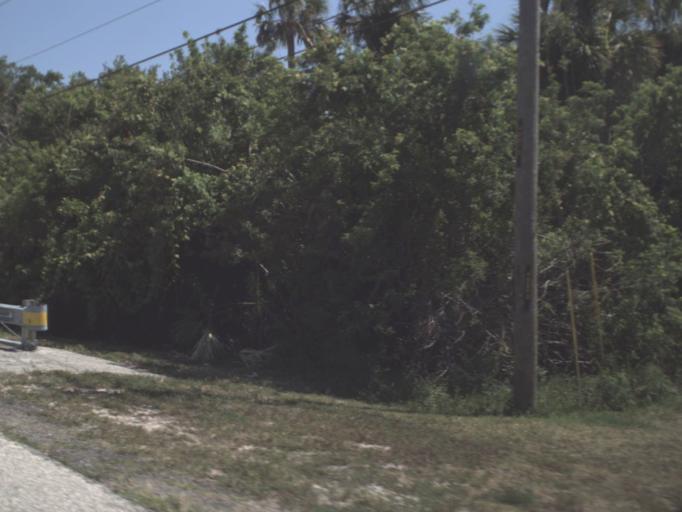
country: US
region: Florida
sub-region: Brevard County
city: Micco
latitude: 27.9105
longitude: -80.5165
